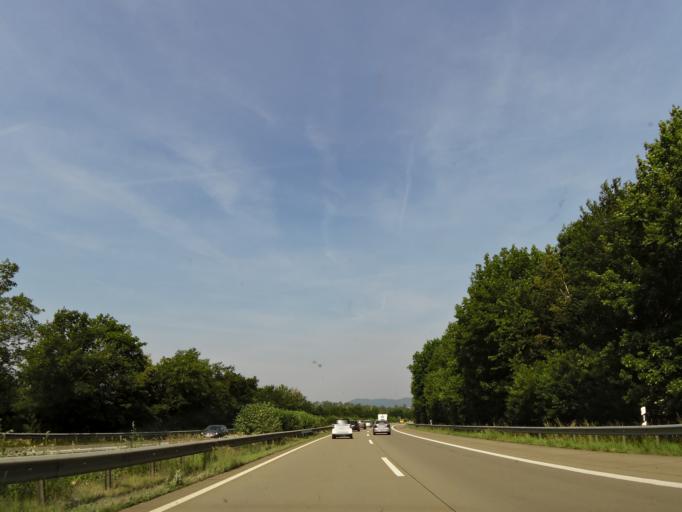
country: DE
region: Rheinland-Pfalz
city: Saffig
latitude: 50.3640
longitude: 7.4290
